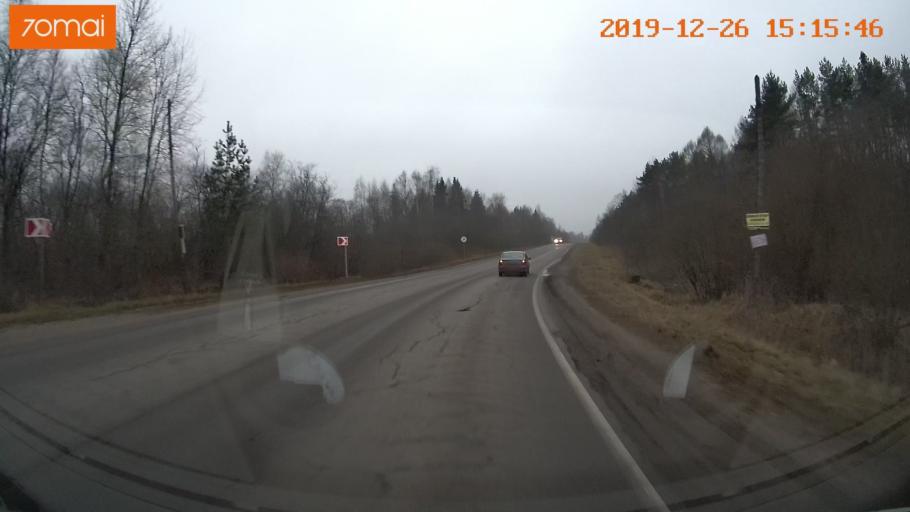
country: RU
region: Jaroslavl
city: Rybinsk
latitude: 58.0933
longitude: 38.8743
